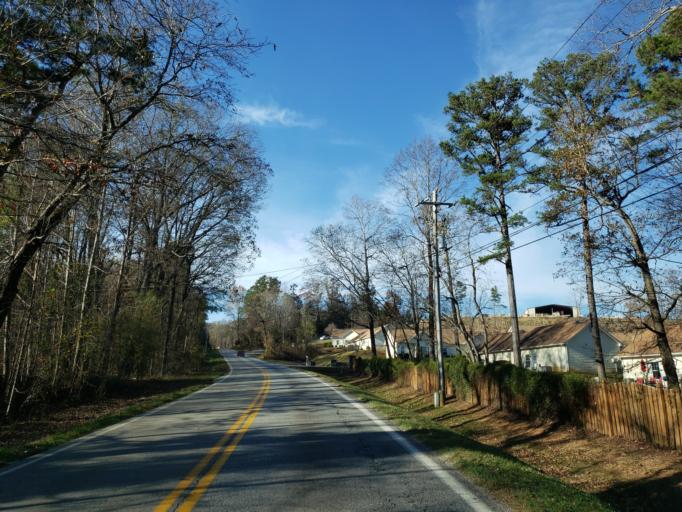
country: US
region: Georgia
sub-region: Lumpkin County
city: Dahlonega
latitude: 34.4496
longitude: -83.9913
